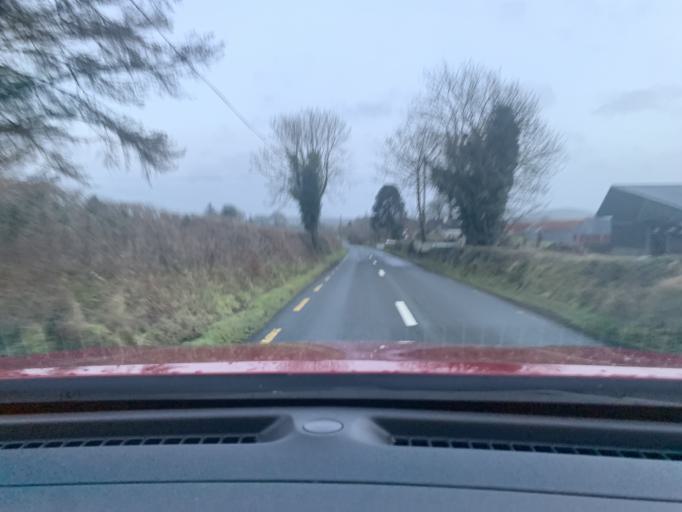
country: IE
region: Connaught
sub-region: Sligo
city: Ballymote
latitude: 54.0313
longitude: -8.4142
